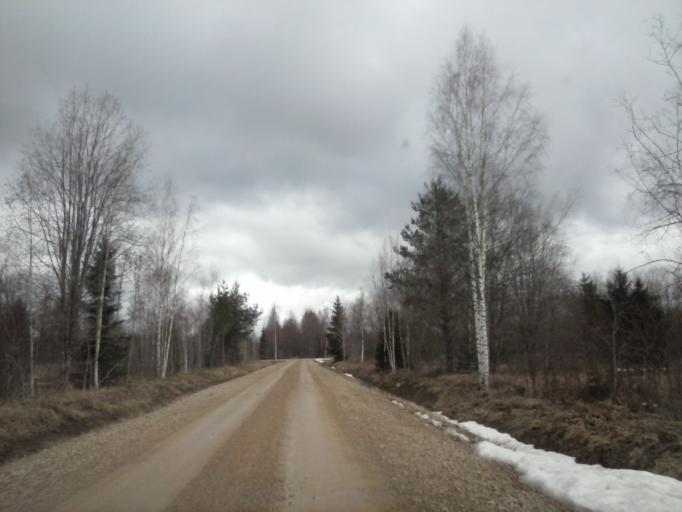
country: EE
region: Jogevamaa
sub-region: Mustvee linn
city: Mustvee
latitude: 59.1053
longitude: 26.8210
